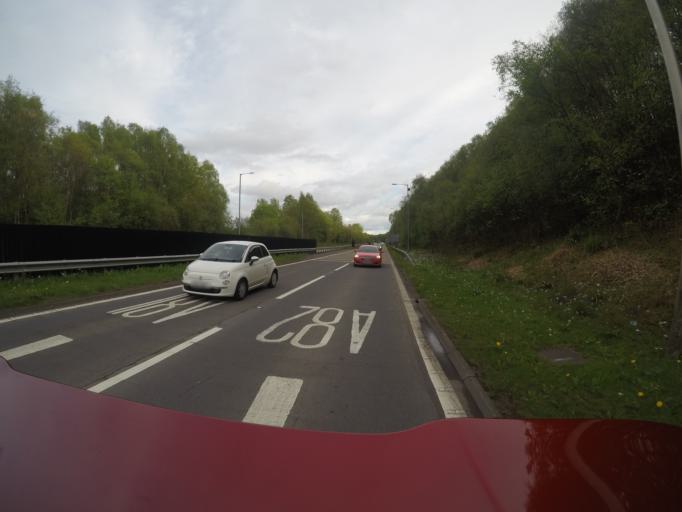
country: GB
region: Scotland
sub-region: West Dunbartonshire
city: Alexandria
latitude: 55.9978
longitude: -4.5970
